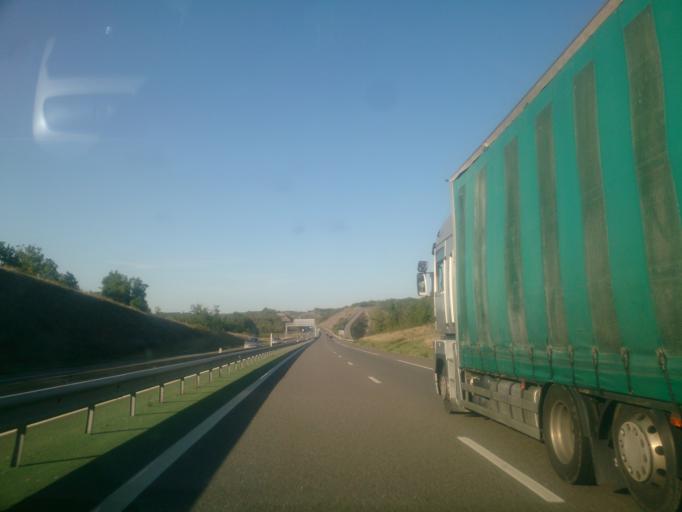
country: FR
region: Midi-Pyrenees
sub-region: Departement du Lot
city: Cahors
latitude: 44.5070
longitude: 1.4987
